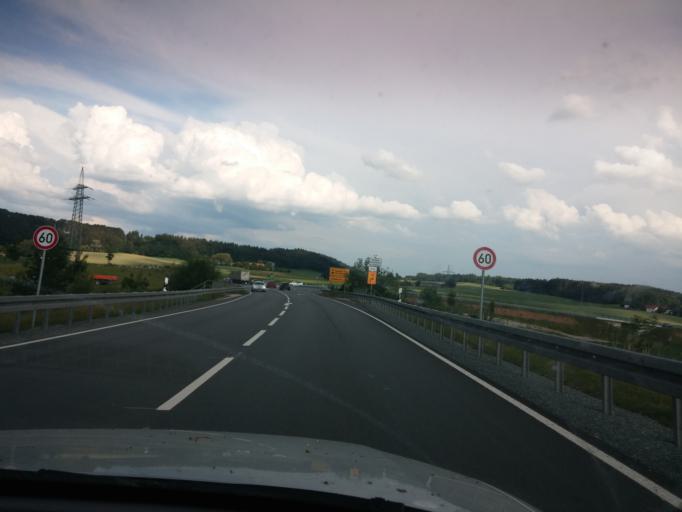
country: DE
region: Bavaria
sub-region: Upper Bavaria
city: Ebersberg
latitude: 48.0626
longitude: 11.9684
